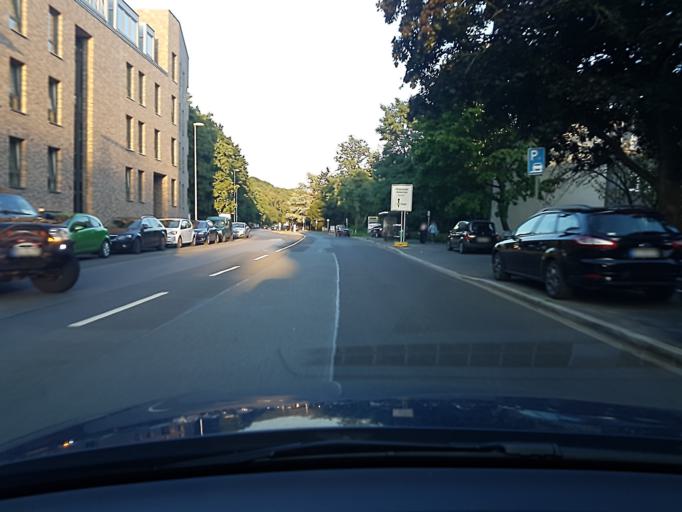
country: DE
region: North Rhine-Westphalia
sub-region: Regierungsbezirk Dusseldorf
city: Ratingen
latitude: 51.2350
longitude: 6.8429
